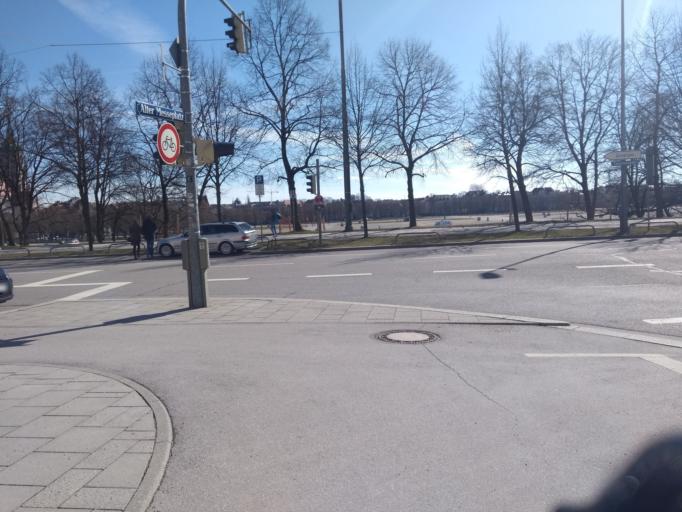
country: DE
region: Bavaria
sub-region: Upper Bavaria
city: Munich
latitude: 48.1344
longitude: 11.5469
